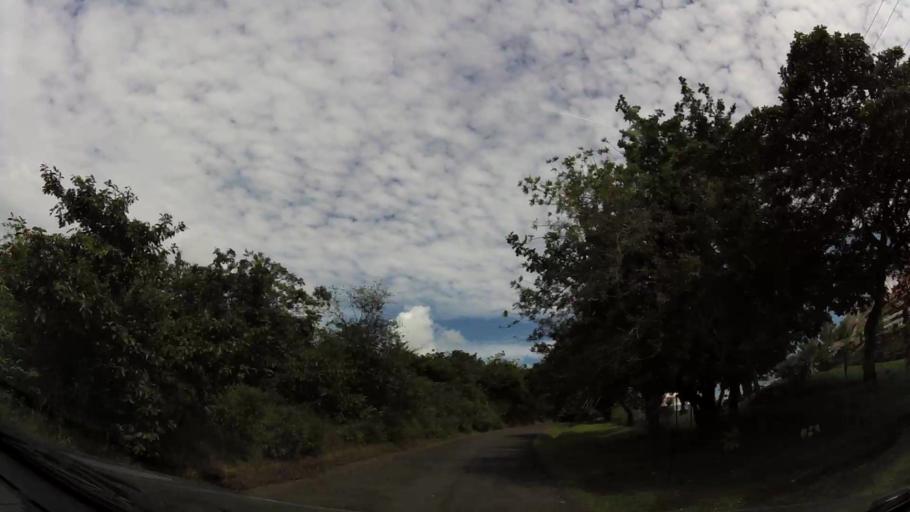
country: PA
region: Panama
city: Nueva Gorgona
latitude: 8.5221
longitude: -79.9140
